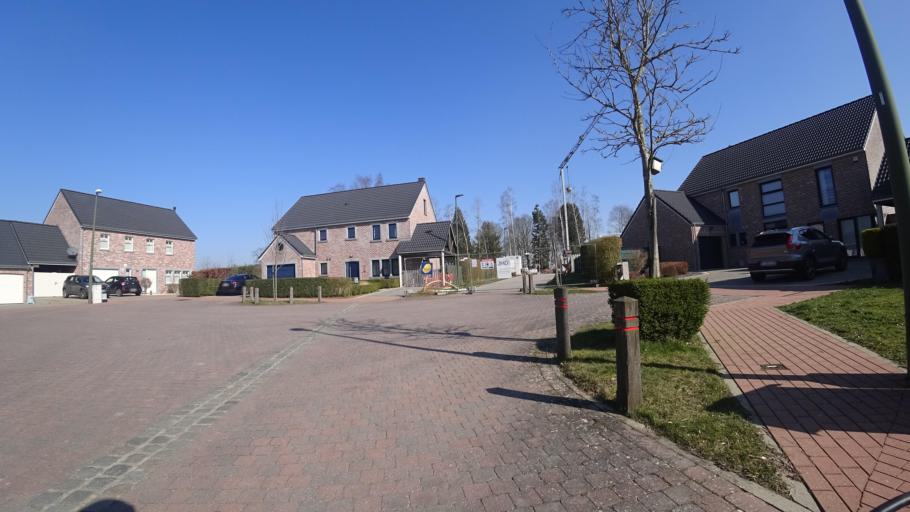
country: BE
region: Wallonia
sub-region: Province du Brabant Wallon
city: Chastre-Villeroux-Blanmont
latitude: 50.6260
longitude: 4.6464
